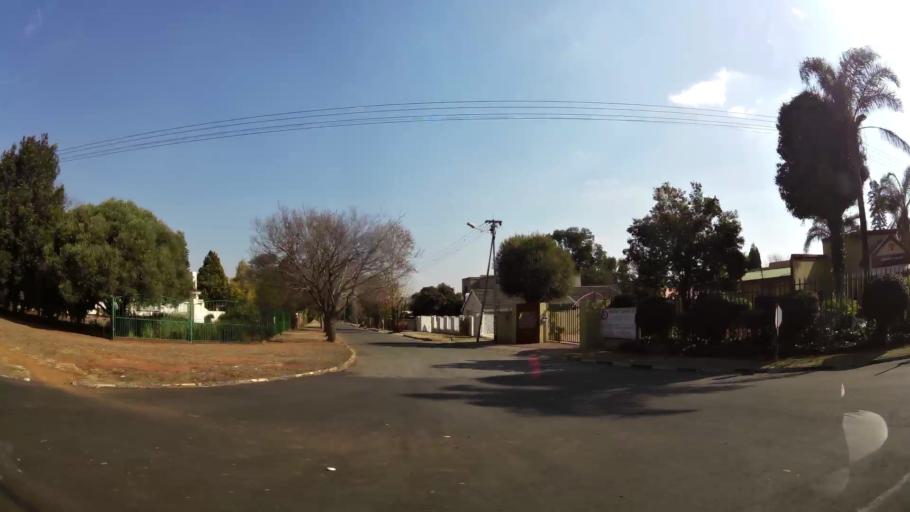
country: ZA
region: Gauteng
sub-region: West Rand District Municipality
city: Randfontein
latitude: -26.1610
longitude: 27.6938
